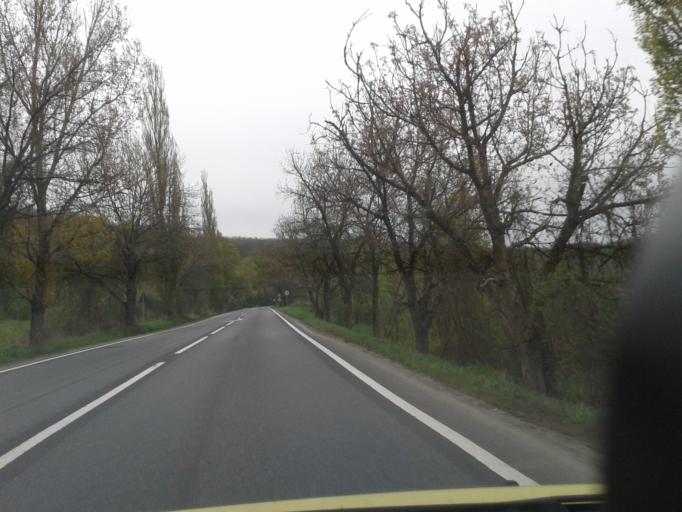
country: RO
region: Arad
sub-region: Comuna Ususau
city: Ususau
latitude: 46.1047
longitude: 21.7848
